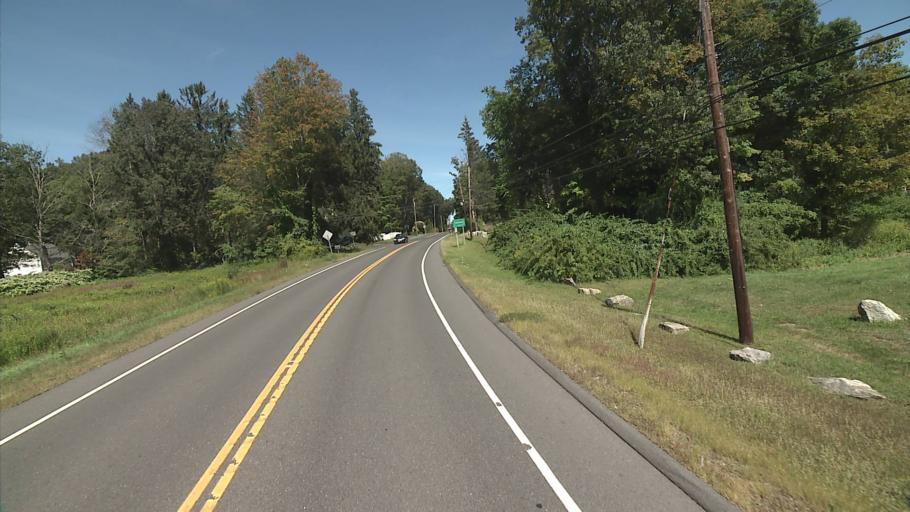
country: US
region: Connecticut
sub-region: New Haven County
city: Southbury
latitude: 41.4593
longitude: -73.1649
